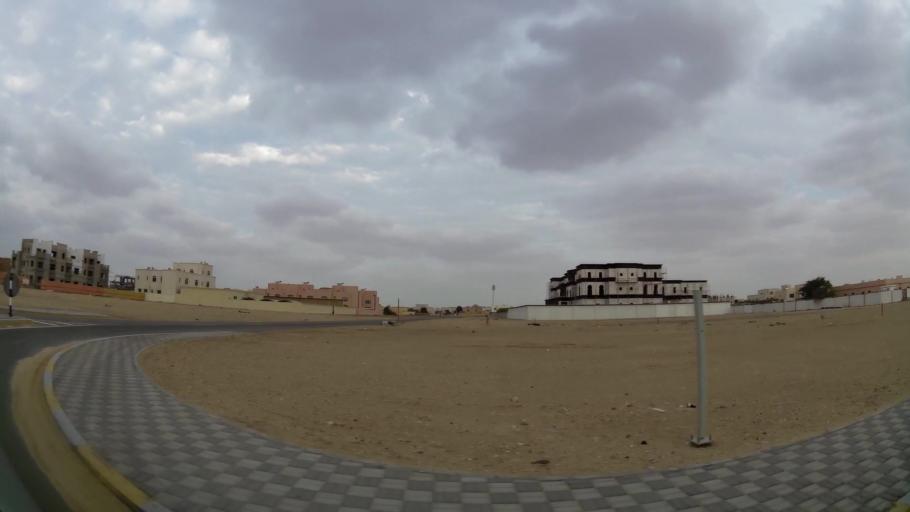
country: AE
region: Abu Dhabi
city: Abu Dhabi
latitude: 24.3557
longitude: 54.5404
